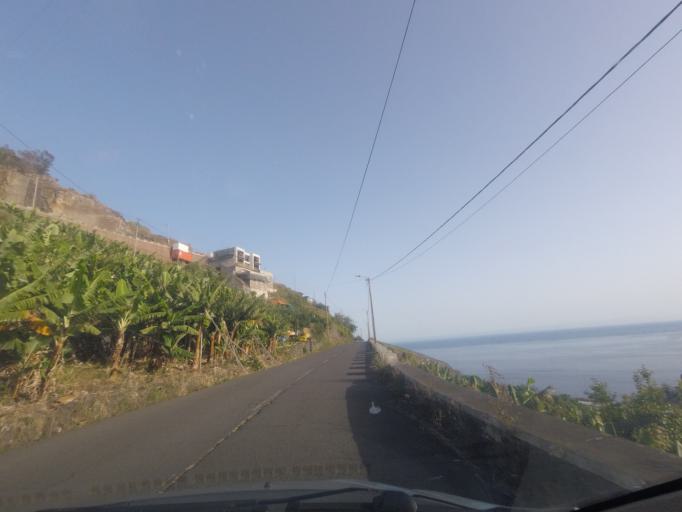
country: PT
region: Madeira
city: Ponta do Sol
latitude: 32.6811
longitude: -17.0728
